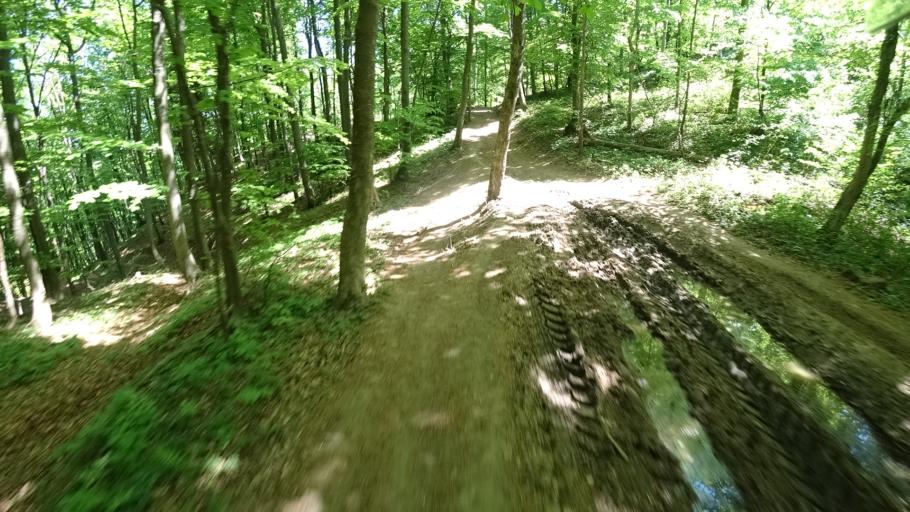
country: HR
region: Zagrebacka
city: Jablanovec
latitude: 45.8686
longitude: 15.8609
